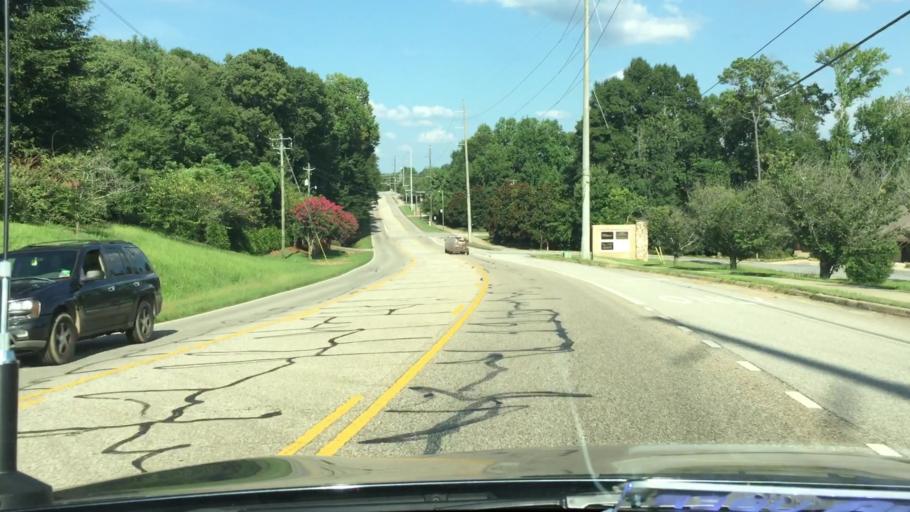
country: US
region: Alabama
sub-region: Lee County
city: Auburn
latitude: 32.5846
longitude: -85.4440
